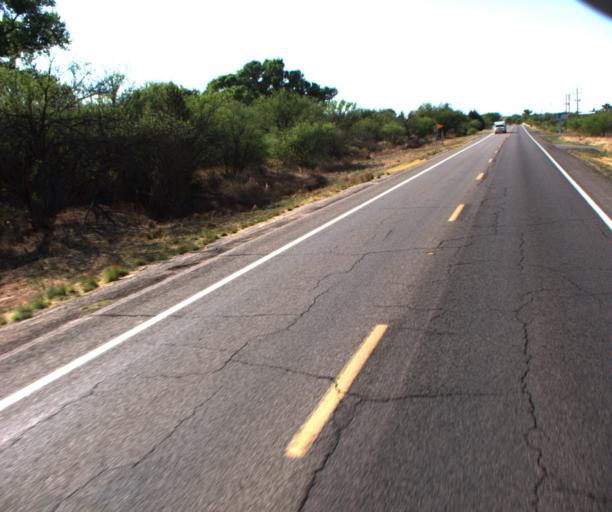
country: US
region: Arizona
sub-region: Cochise County
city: Saint David
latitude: 31.8727
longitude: -110.2092
